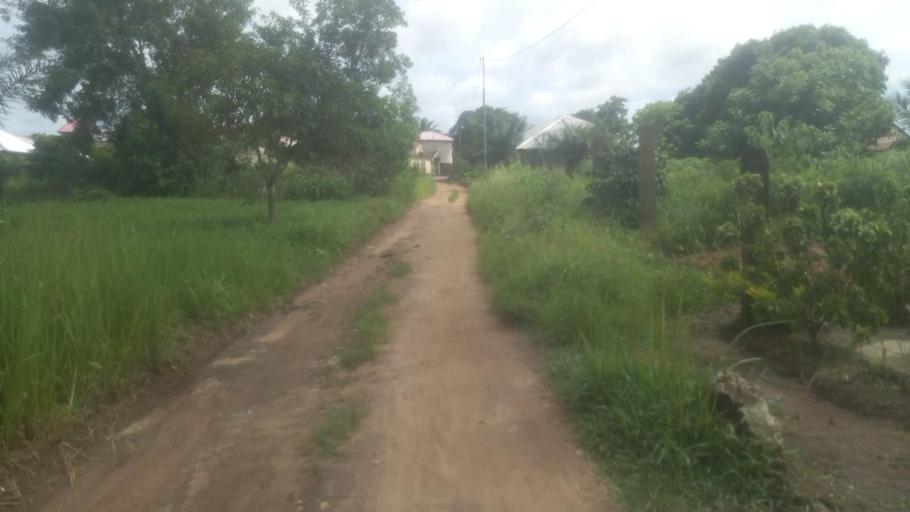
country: SL
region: Northern Province
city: Masoyila
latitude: 8.5939
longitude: -13.1871
